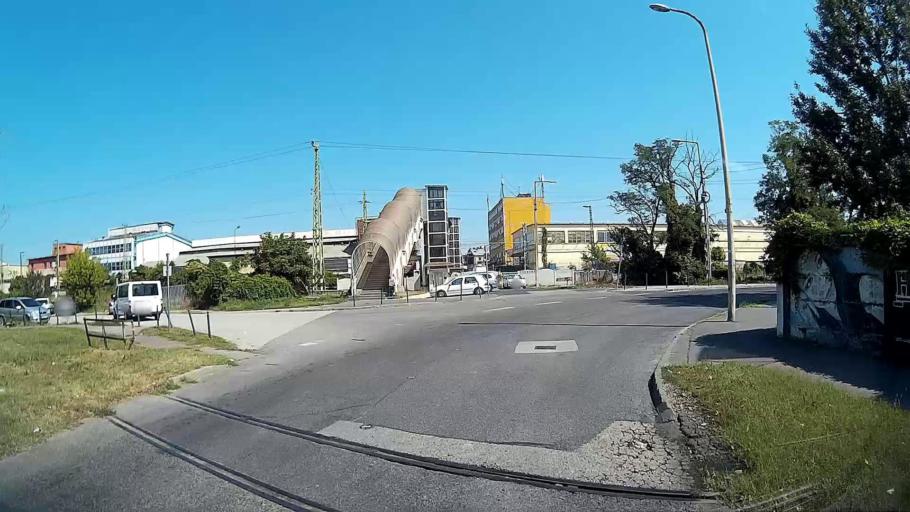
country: HU
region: Budapest
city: Budapest XVIII. keruelet
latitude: 47.4563
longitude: 19.1760
